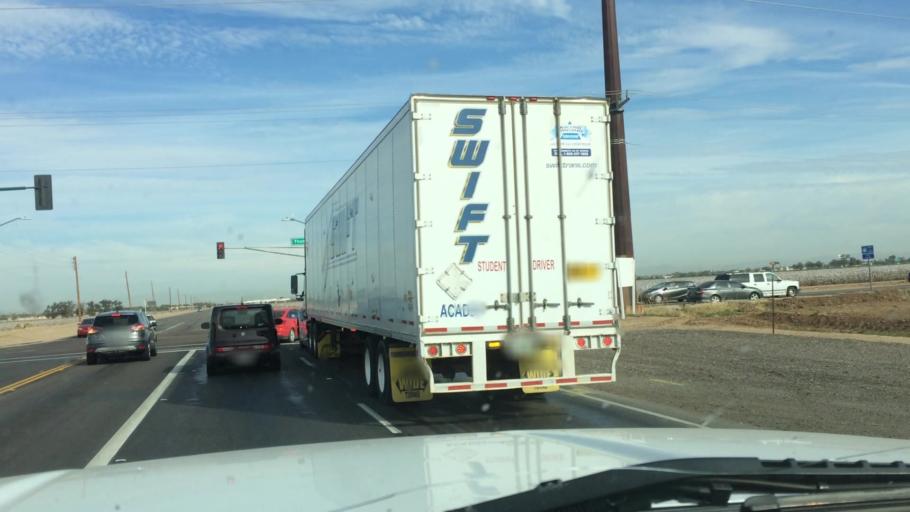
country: US
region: Arizona
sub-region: Maricopa County
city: Tolleson
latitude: 33.4788
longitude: -112.2724
